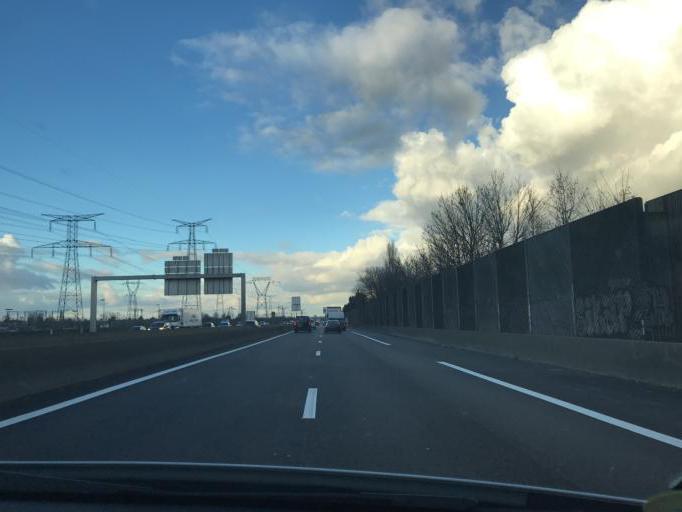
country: FR
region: Ile-de-France
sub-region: Departement de Seine-et-Marne
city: Collegien
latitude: 48.8376
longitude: 2.6650
